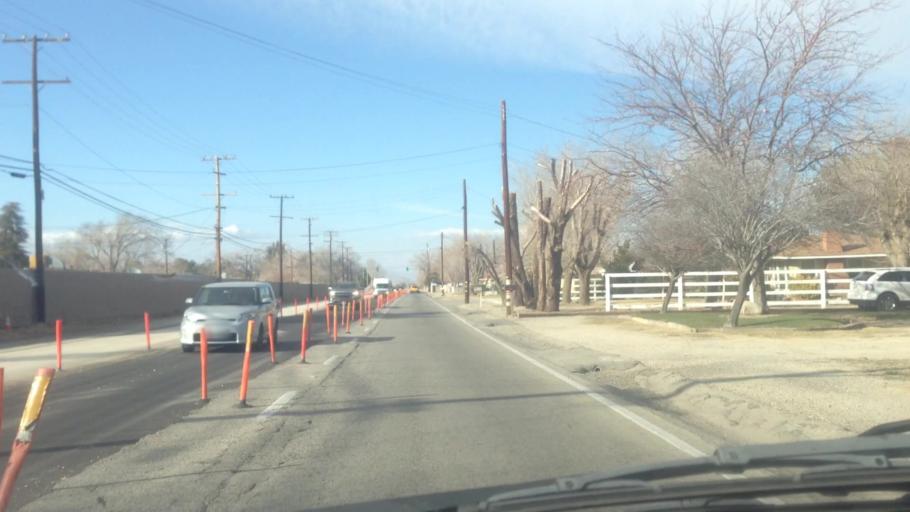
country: US
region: California
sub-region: Los Angeles County
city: Lancaster
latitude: 34.6941
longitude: -118.1657
